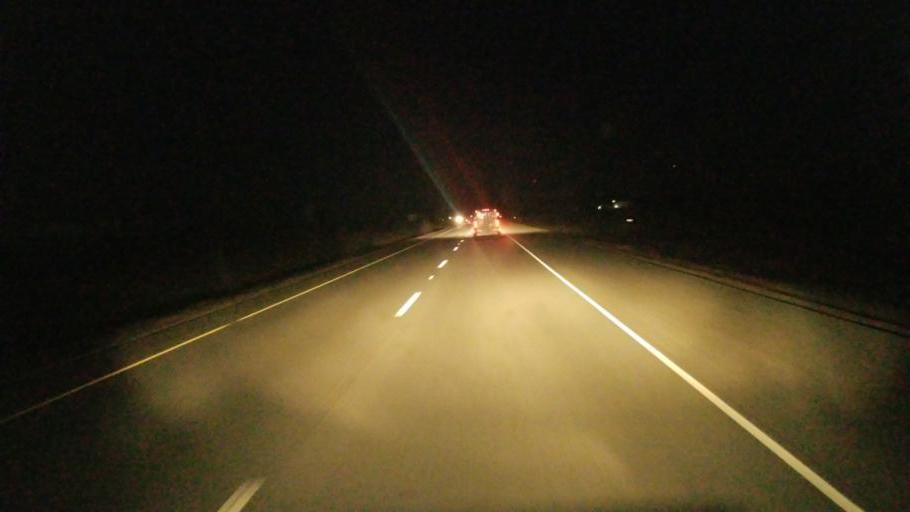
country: US
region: Illinois
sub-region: Henderson County
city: Oquawka
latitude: 40.8473
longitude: -90.9146
